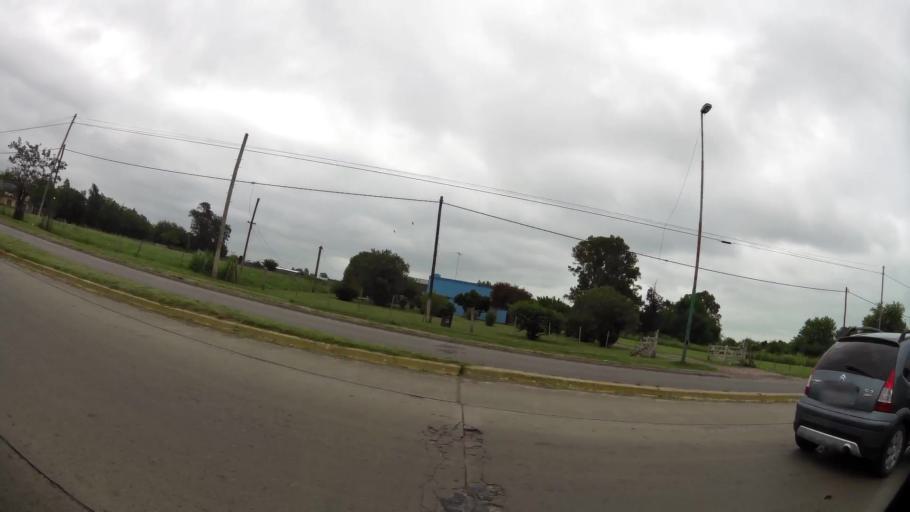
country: AR
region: Buenos Aires
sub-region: Partido de La Plata
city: La Plata
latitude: -34.9929
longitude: -58.0454
